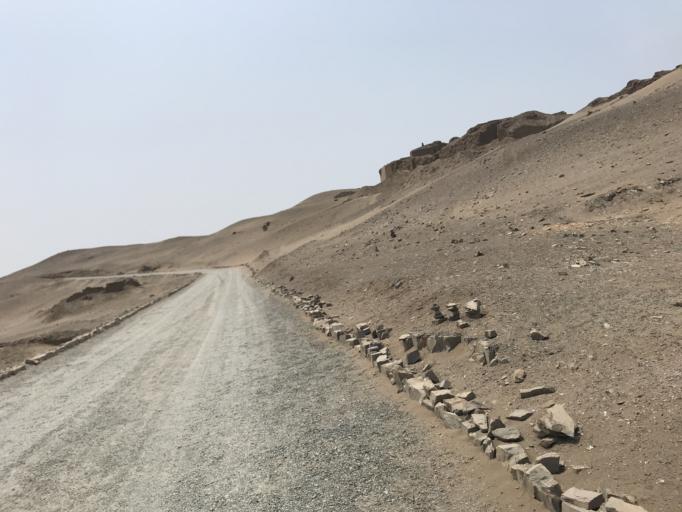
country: PE
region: Lima
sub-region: Lima
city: Punta Hermosa
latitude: -12.2547
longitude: -76.8984
